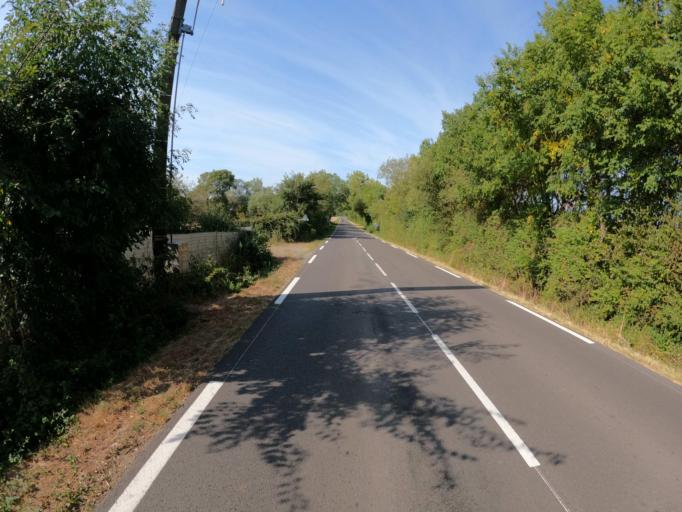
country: FR
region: Pays de la Loire
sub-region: Departement de la Vendee
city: Saint-Christophe-du-Ligneron
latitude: 46.8162
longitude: -1.7686
